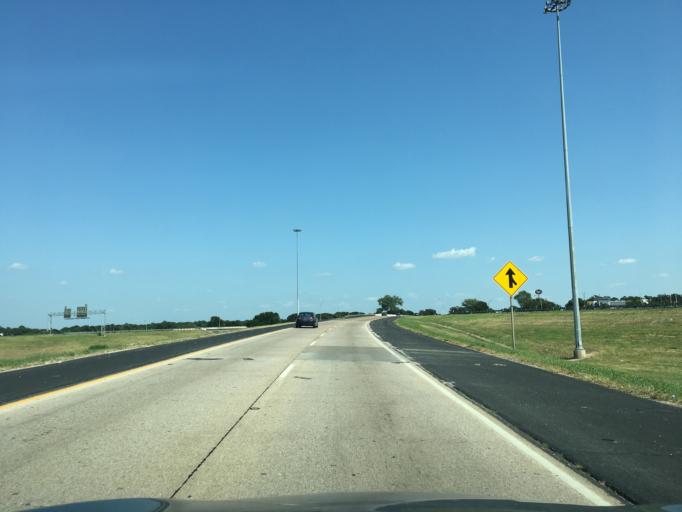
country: US
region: Texas
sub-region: Tarrant County
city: Kennedale
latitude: 32.6686
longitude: -97.2075
